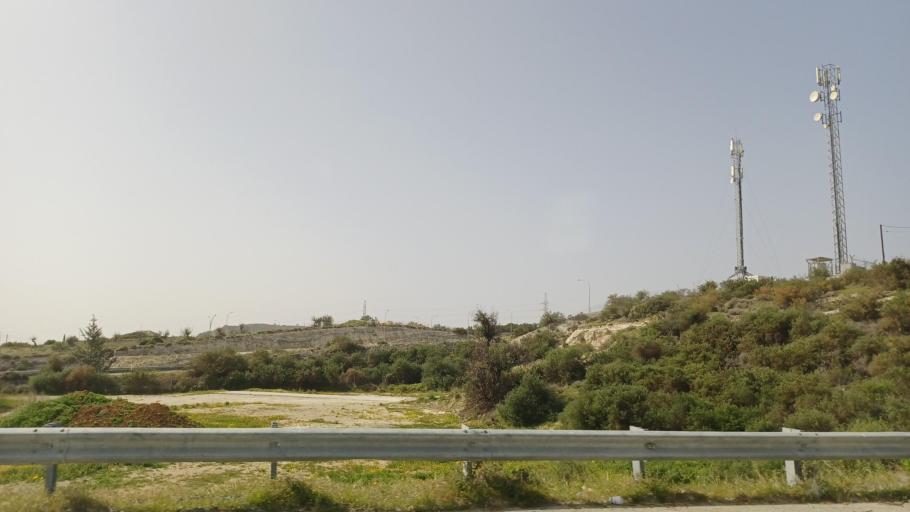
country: CY
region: Limassol
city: Pissouri
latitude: 34.6846
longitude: 32.6995
